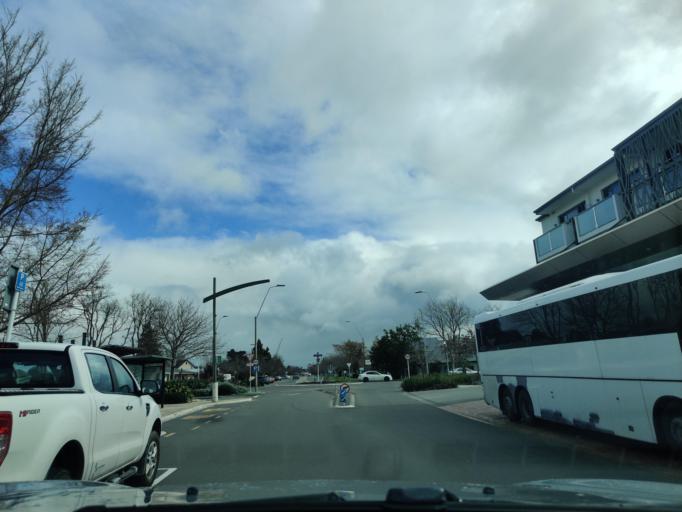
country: NZ
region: Hawke's Bay
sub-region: Hastings District
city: Hastings
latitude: -39.6704
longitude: 176.8765
